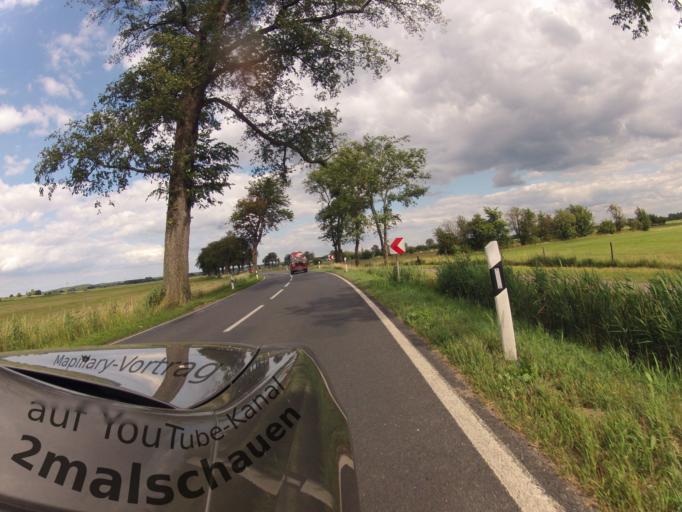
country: DE
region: Mecklenburg-Vorpommern
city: Usedom
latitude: 53.8740
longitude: 13.8901
